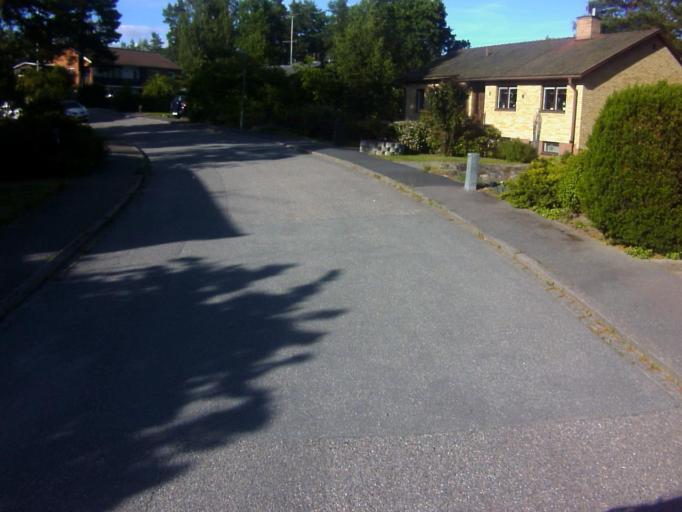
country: SE
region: Soedermanland
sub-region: Eskilstuna Kommun
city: Eskilstuna
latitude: 59.3603
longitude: 16.4904
